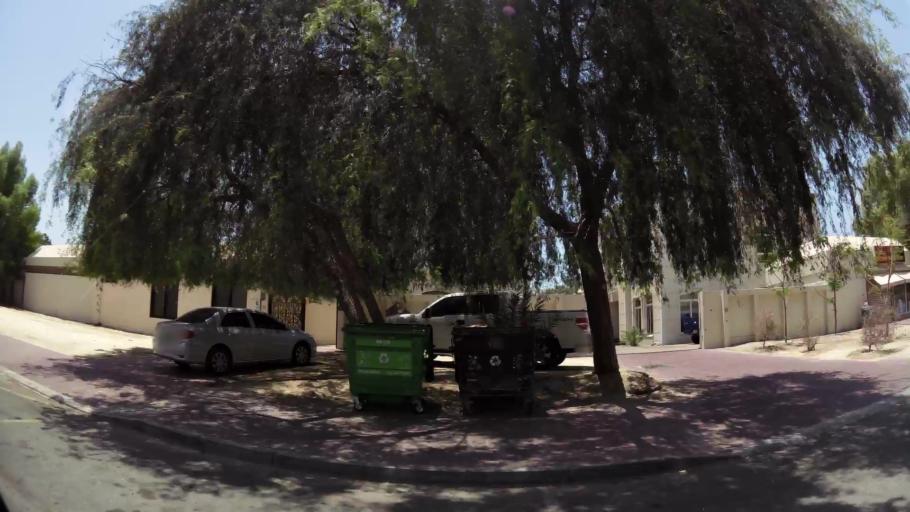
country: AE
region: Dubai
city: Dubai
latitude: 25.2078
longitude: 55.2505
